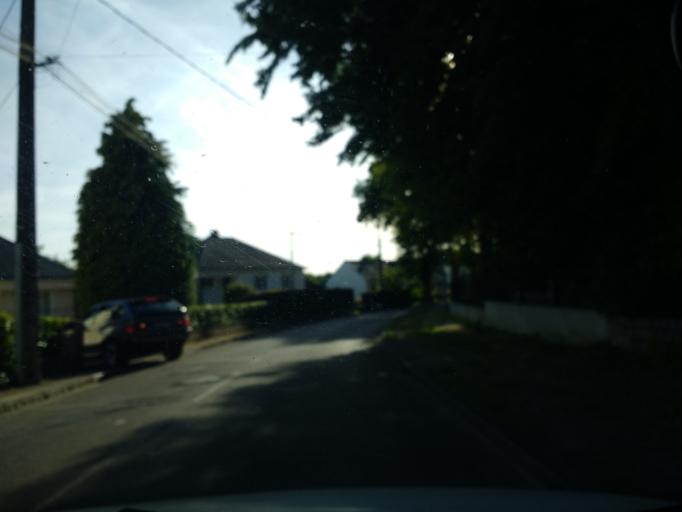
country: FR
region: Pays de la Loire
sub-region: Departement de la Loire-Atlantique
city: Orvault
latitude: 47.2633
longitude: -1.5909
